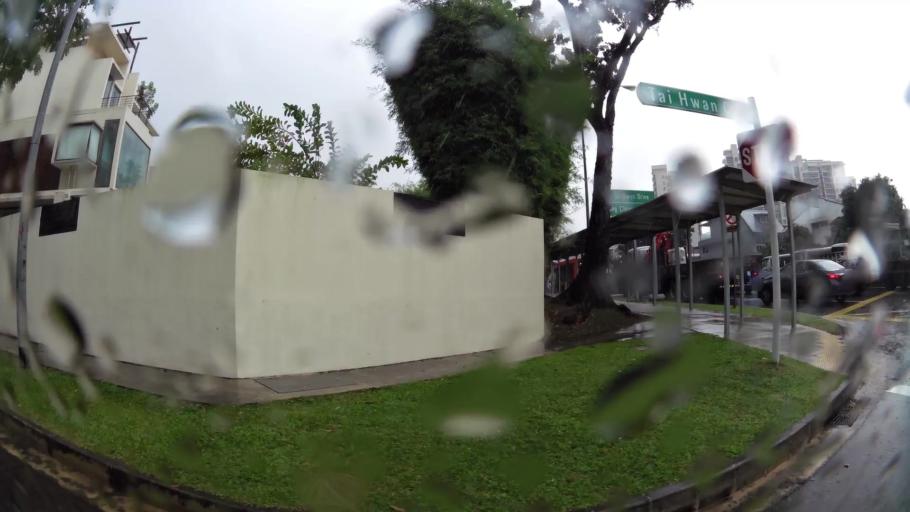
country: SG
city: Singapore
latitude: 1.3547
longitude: 103.8611
